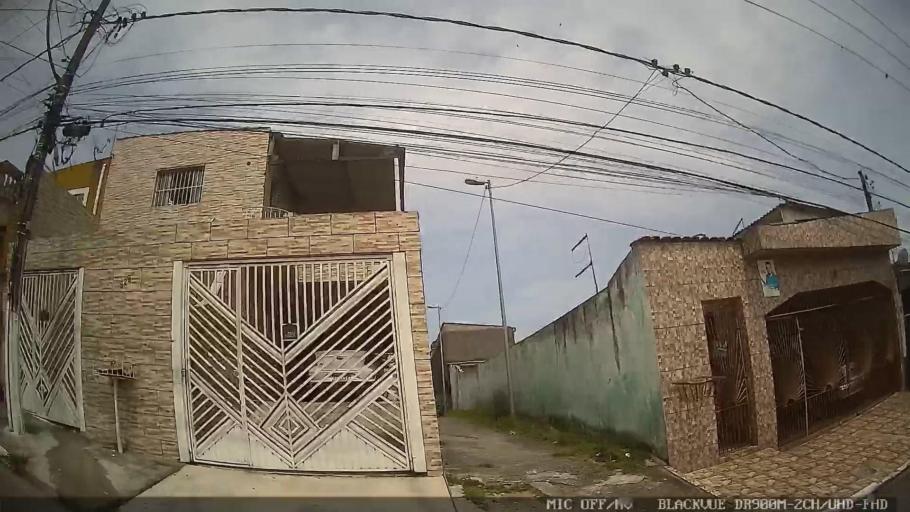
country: BR
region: Sao Paulo
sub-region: Poa
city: Poa
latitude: -23.5233
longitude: -46.3618
